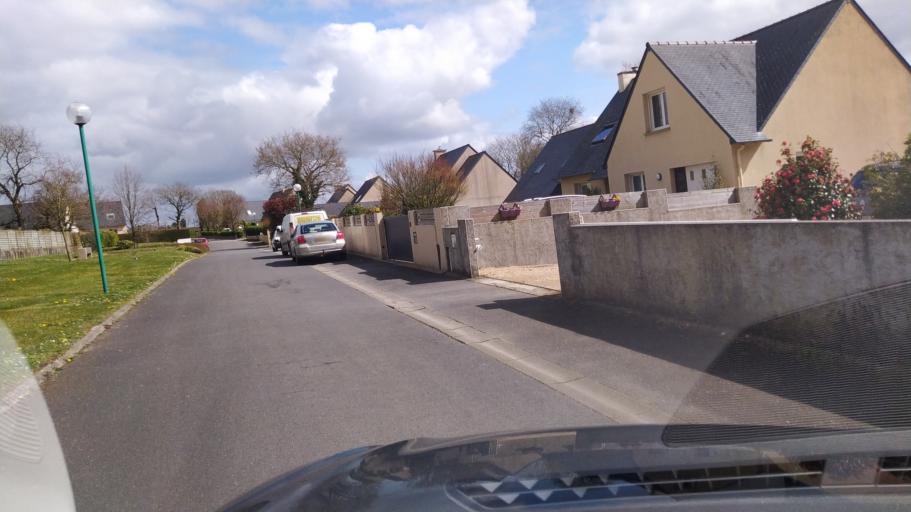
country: FR
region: Brittany
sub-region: Departement du Finistere
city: Bodilis
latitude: 48.5280
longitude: -4.1119
